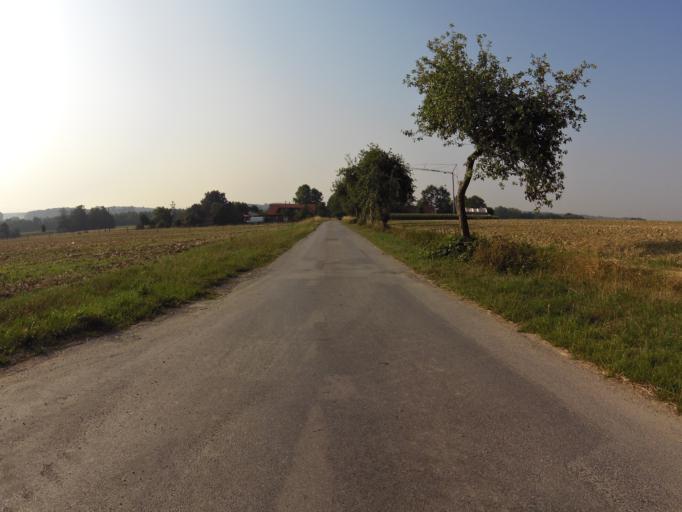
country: DE
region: North Rhine-Westphalia
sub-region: Regierungsbezirk Munster
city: Billerbeck
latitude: 51.9802
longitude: 7.3229
